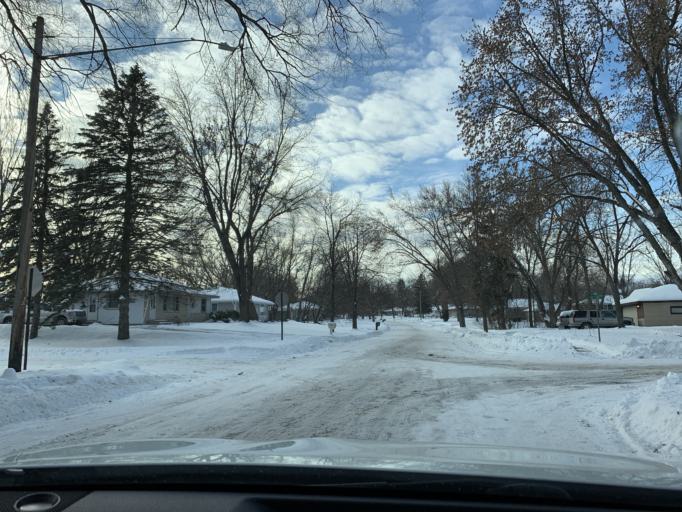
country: US
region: Minnesota
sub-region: Anoka County
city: Blaine
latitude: 45.1717
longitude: -93.2852
